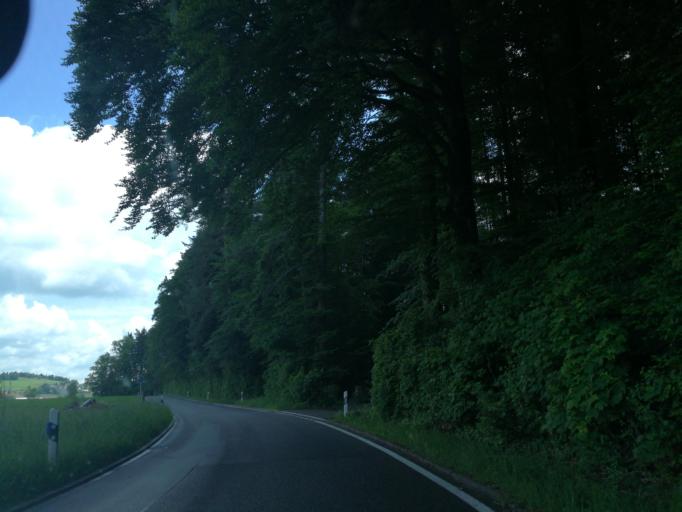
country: CH
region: Zurich
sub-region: Bezirk Meilen
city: Zumikon
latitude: 47.3132
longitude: 8.6238
